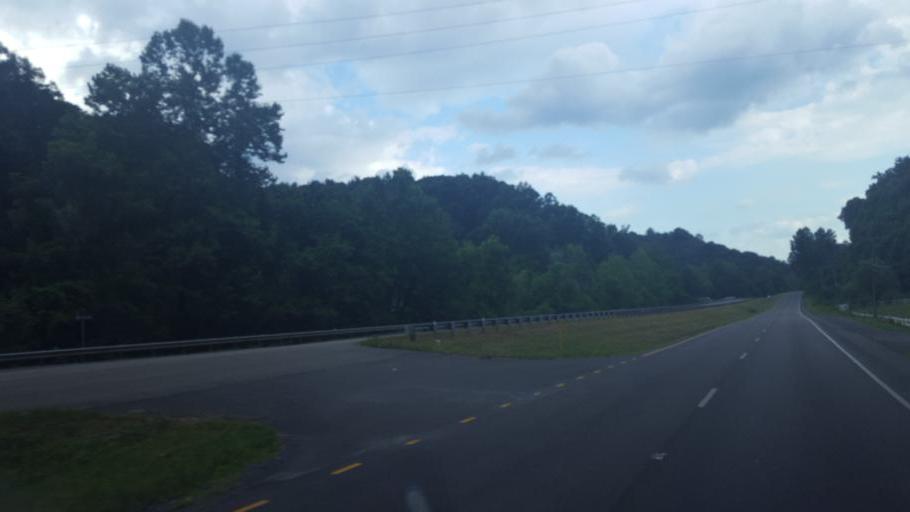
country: US
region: Virginia
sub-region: Wise County
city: Pound
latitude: 37.0857
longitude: -82.5988
